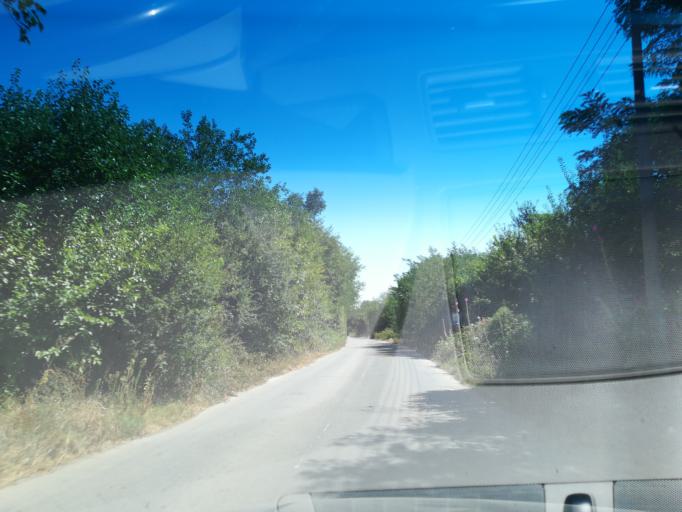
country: BG
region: Pazardzhik
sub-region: Obshtina Pazardzhik
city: Pazardzhik
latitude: 42.2635
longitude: 24.4089
